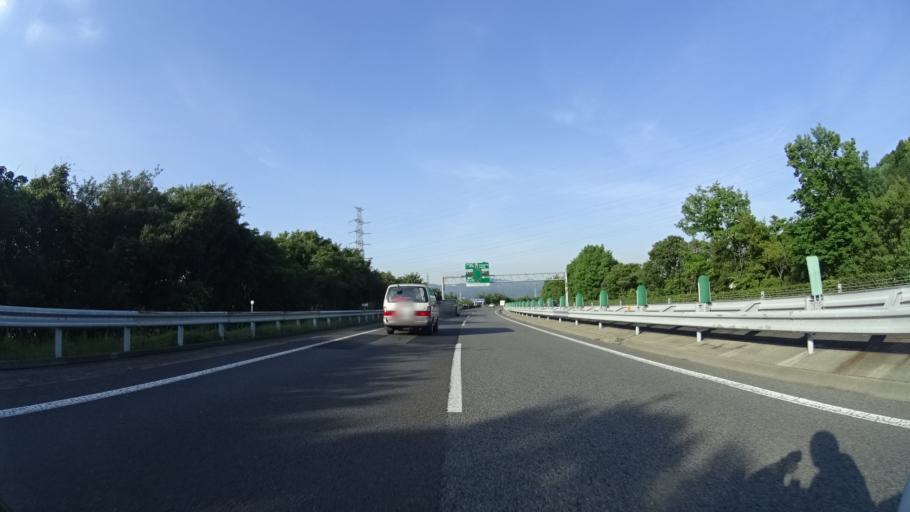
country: JP
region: Ehime
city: Kawanoecho
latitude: 33.9737
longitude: 133.5583
